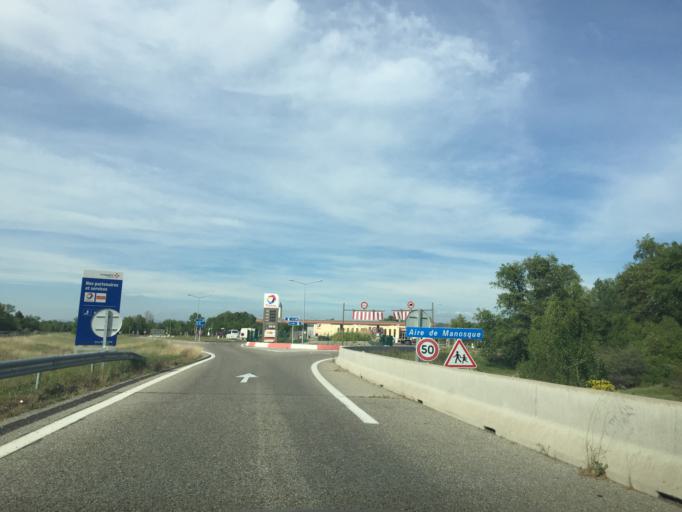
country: FR
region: Provence-Alpes-Cote d'Azur
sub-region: Departement des Alpes-de-Haute-Provence
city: Volx
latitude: 43.8407
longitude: 5.8487
